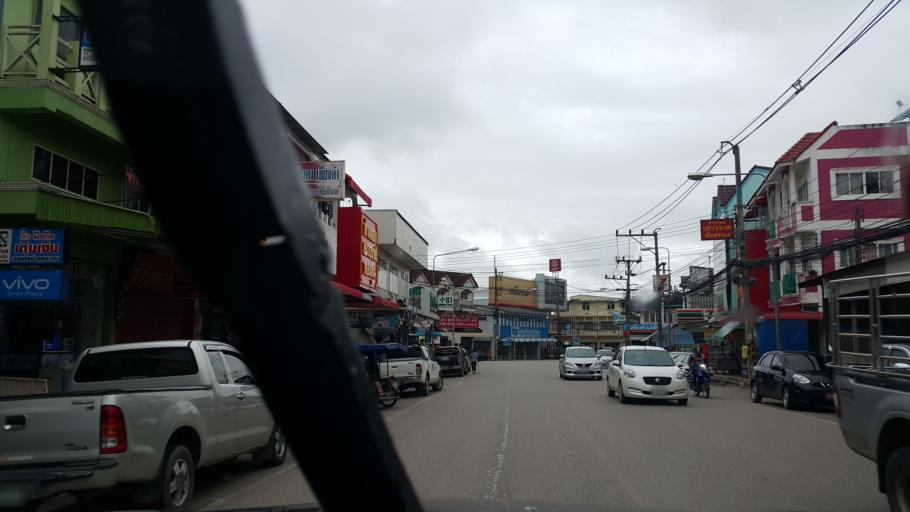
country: TH
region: Phayao
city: Chiang Kham
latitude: 19.5256
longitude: 100.3034
